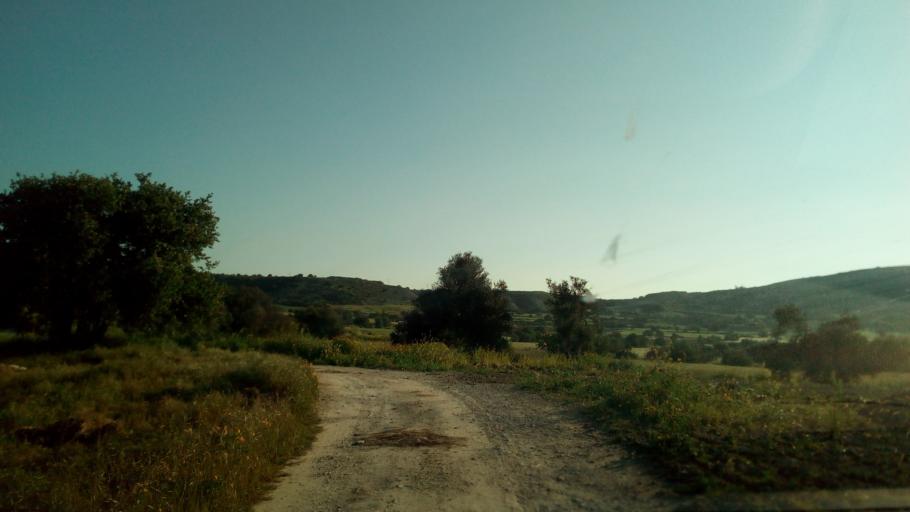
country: CY
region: Larnaka
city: Kofinou
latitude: 34.8393
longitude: 33.4479
